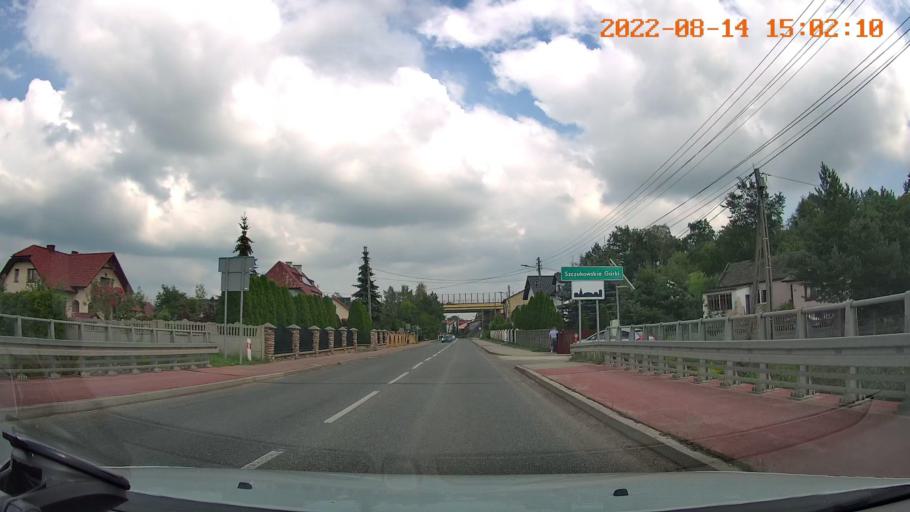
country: PL
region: Swietokrzyskie
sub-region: Powiat kielecki
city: Piekoszow
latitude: 50.8824
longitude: 20.5188
